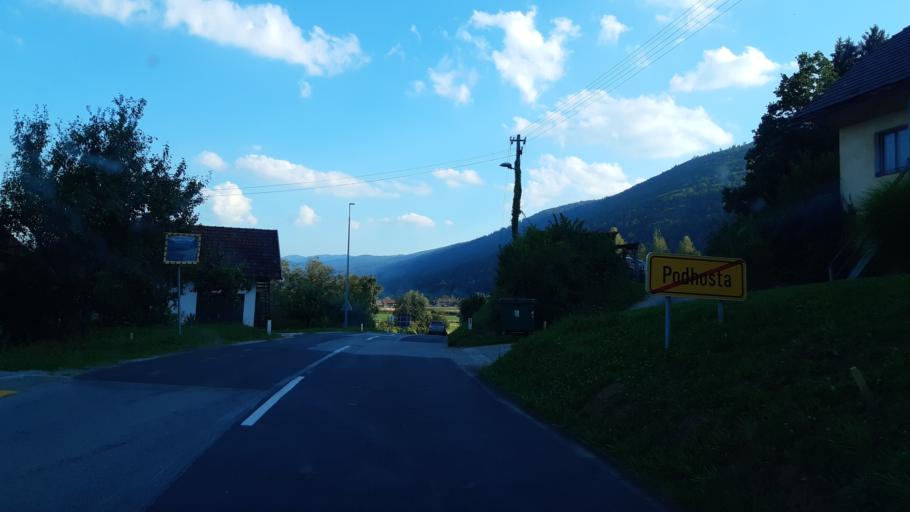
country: SI
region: Dolenjske Toplice
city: Dolenjske Toplice
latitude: 45.7584
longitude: 15.0328
